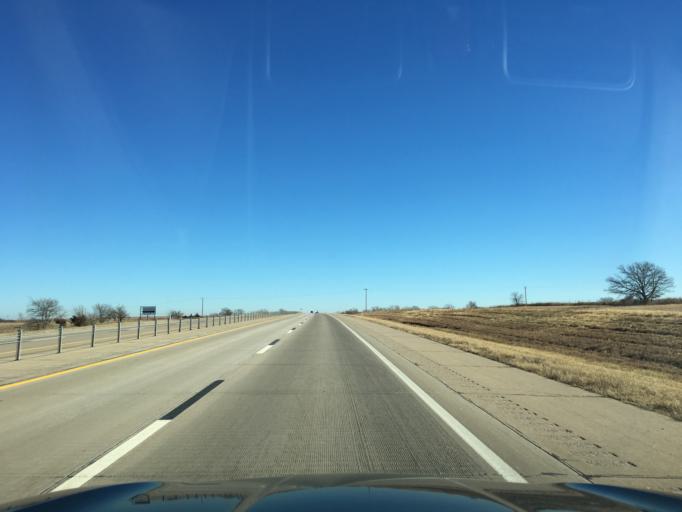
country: US
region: Oklahoma
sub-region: Noble County
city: Perry
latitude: 36.3920
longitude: -97.1825
